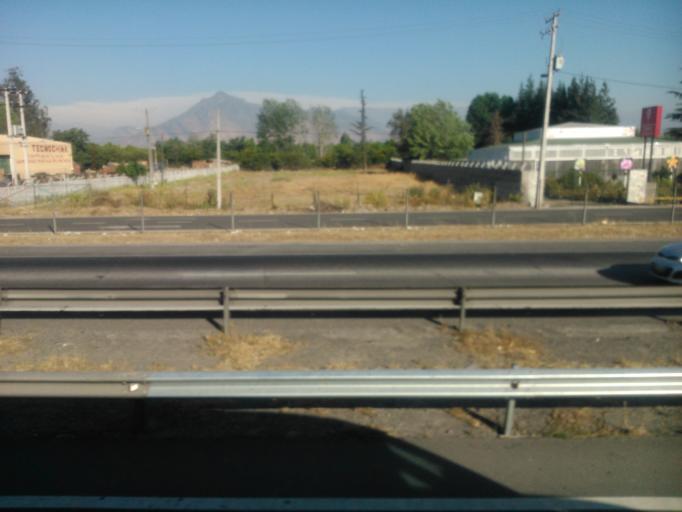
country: CL
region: Santiago Metropolitan
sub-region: Provincia de Maipo
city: Buin
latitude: -33.7213
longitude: -70.7279
